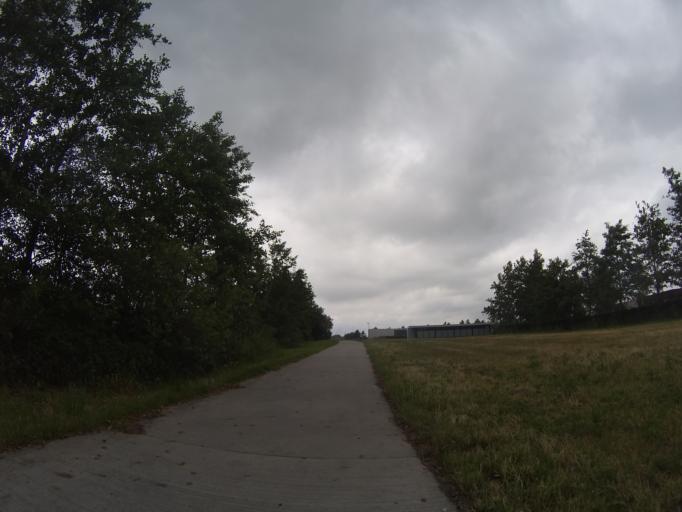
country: NL
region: Drenthe
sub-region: Gemeente Emmen
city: Klazienaveen
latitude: 52.7300
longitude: 6.9641
